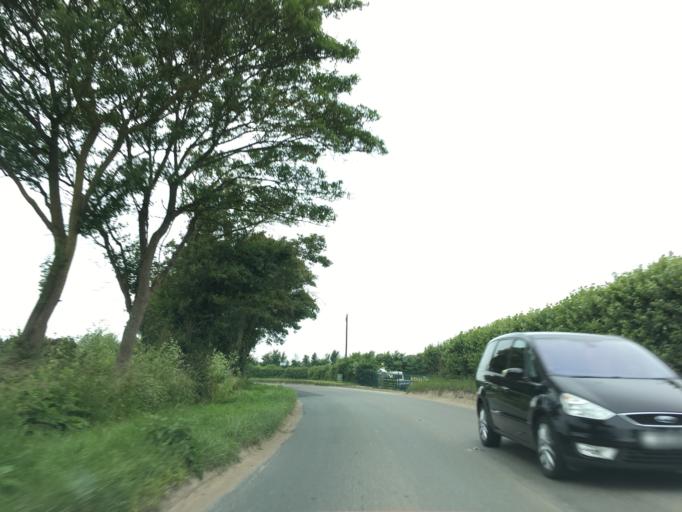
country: GB
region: England
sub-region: Gloucestershire
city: Stonehouse
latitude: 51.7607
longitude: -2.3425
